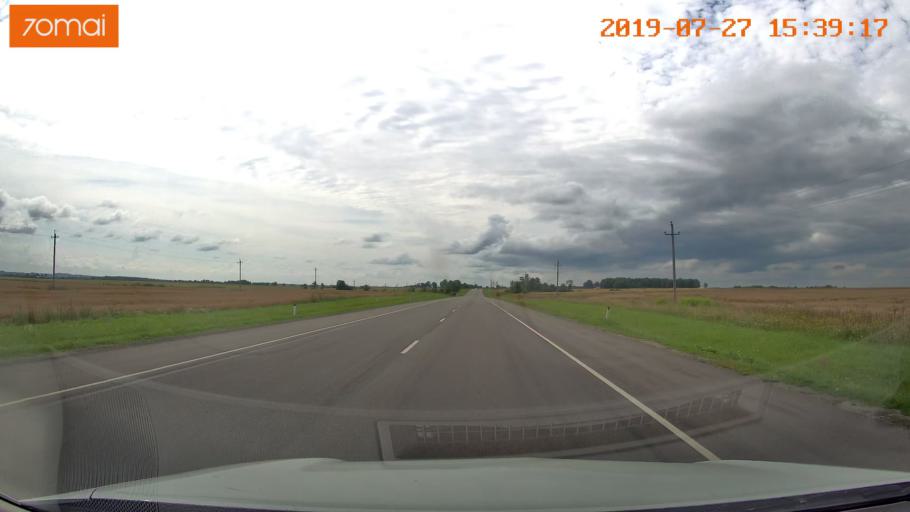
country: RU
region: Kaliningrad
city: Gusev
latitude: 54.6059
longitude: 22.2914
